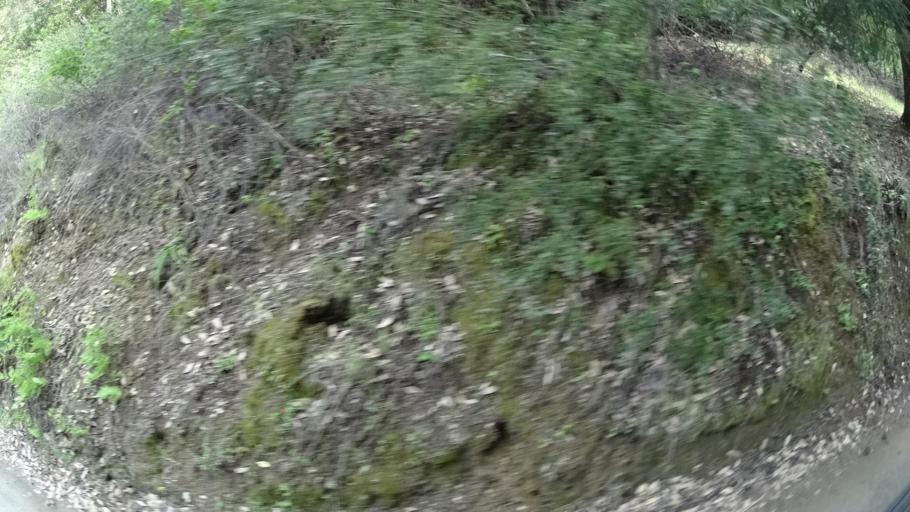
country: US
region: California
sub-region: Humboldt County
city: Redway
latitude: 40.0391
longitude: -123.8431
